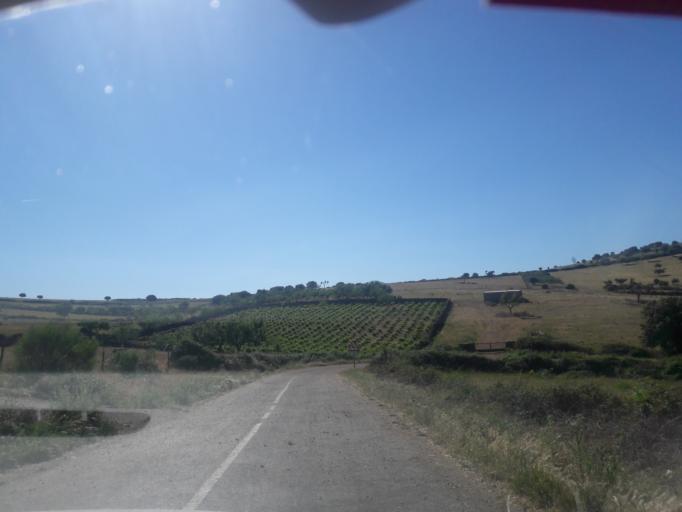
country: ES
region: Castille and Leon
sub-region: Provincia de Salamanca
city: Saucelle
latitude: 41.0406
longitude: -6.7603
